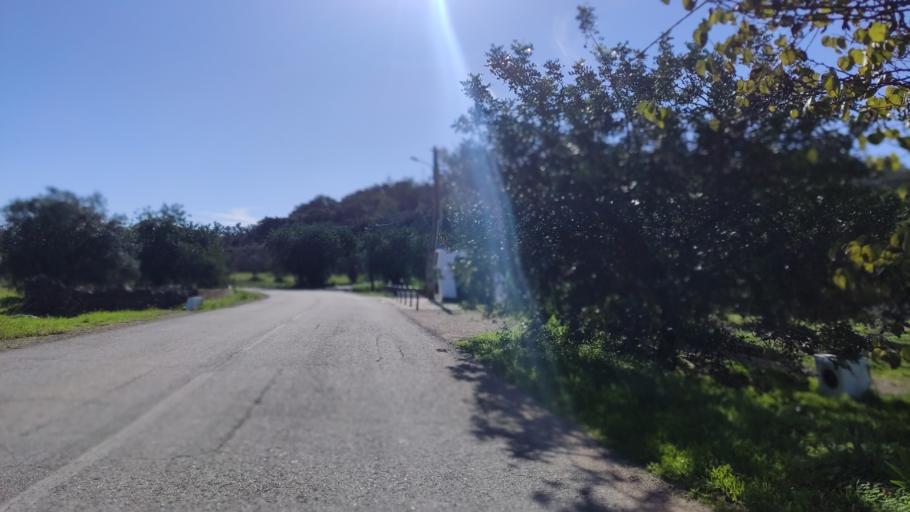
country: PT
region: Faro
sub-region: Sao Bras de Alportel
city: Sao Bras de Alportel
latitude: 37.1534
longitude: -7.8562
